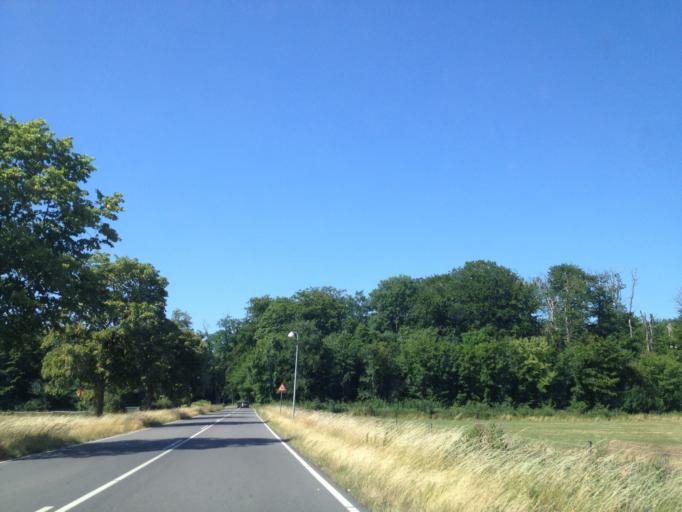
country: DK
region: Capital Region
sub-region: Fredensborg Kommune
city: Niva
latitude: 55.9209
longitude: 12.5114
